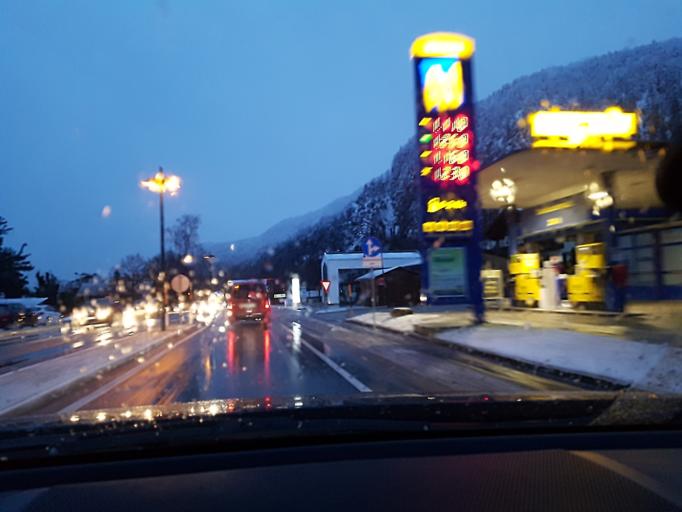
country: AT
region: Salzburg
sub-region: Politischer Bezirk Salzburg-Umgebung
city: Sankt Gilgen
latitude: 47.7646
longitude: 13.3643
